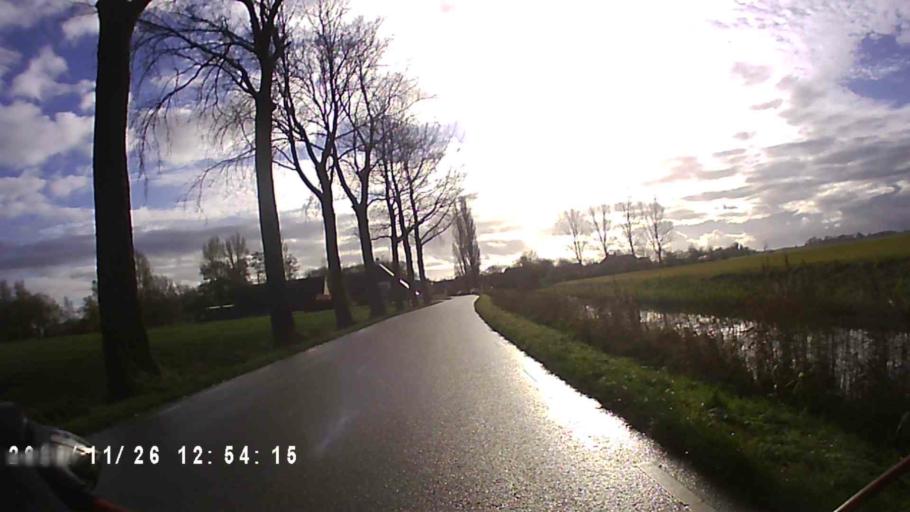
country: NL
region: Groningen
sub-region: Gemeente Appingedam
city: Appingedam
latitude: 53.3487
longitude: 6.7941
